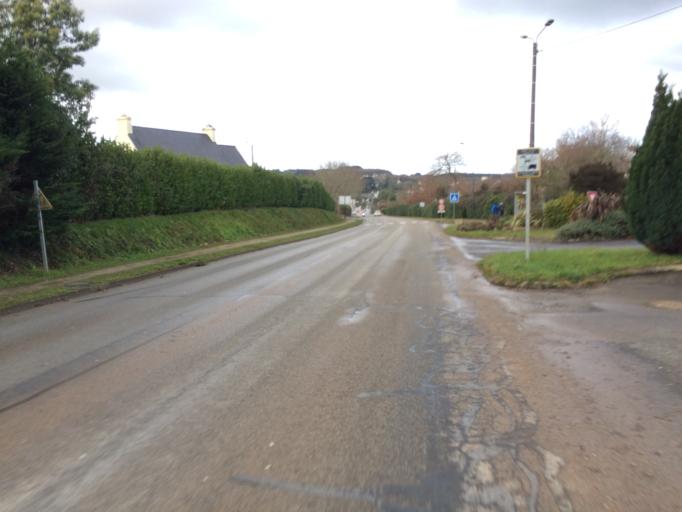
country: FR
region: Brittany
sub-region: Departement du Finistere
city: Daoulas
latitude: 48.3537
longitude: -4.2556
